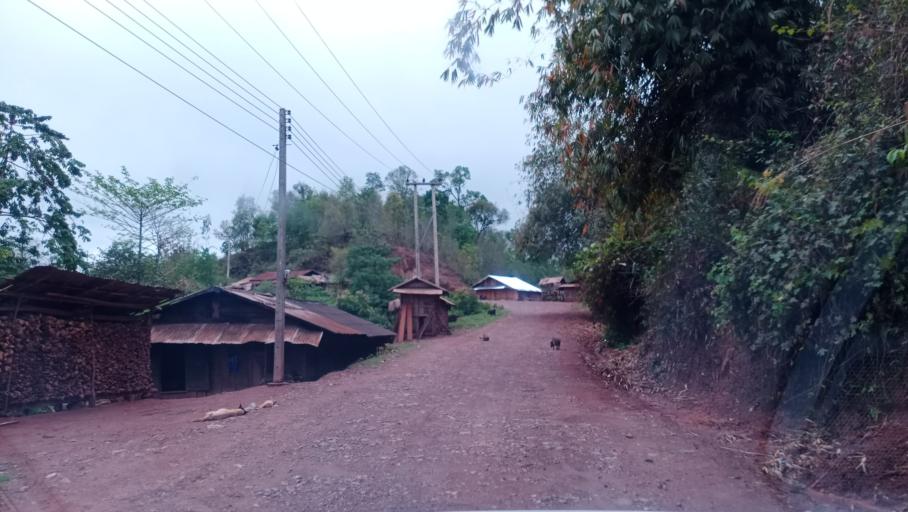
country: LA
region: Phongsali
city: Phongsali
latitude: 21.3388
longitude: 102.0804
